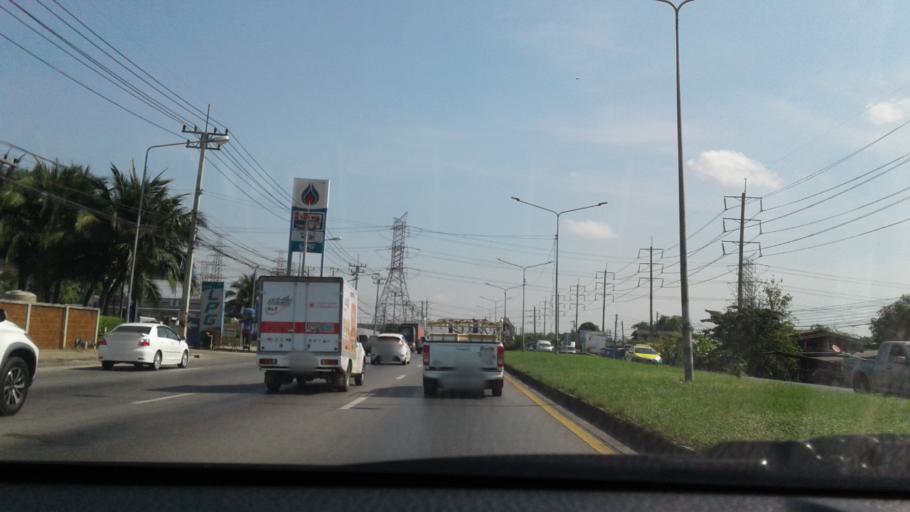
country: TH
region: Phra Nakhon Si Ayutthaya
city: Ban Bang Kadi Pathum Thani
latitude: 13.9714
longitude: 100.5637
